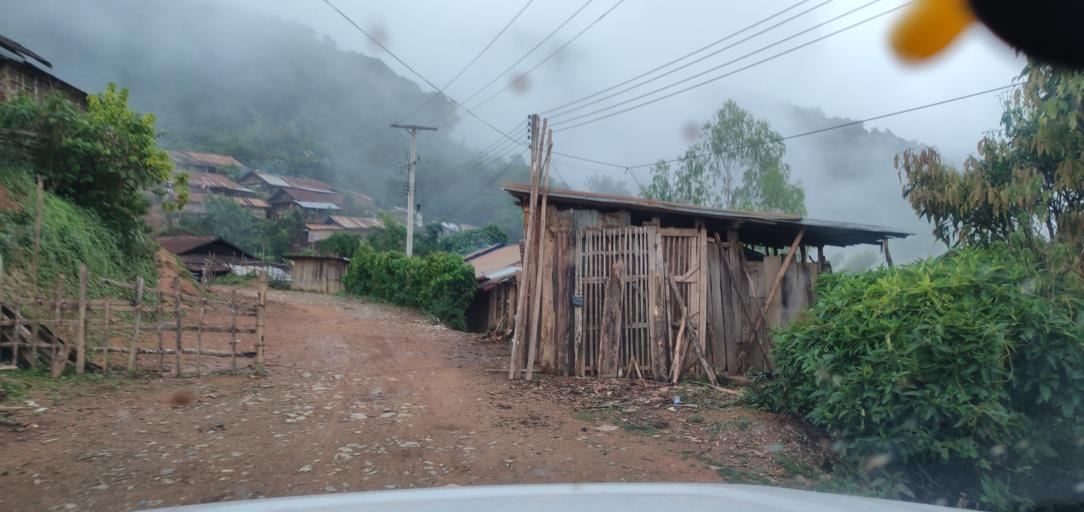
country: LA
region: Phongsali
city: Phongsali
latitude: 21.4418
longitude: 102.2957
